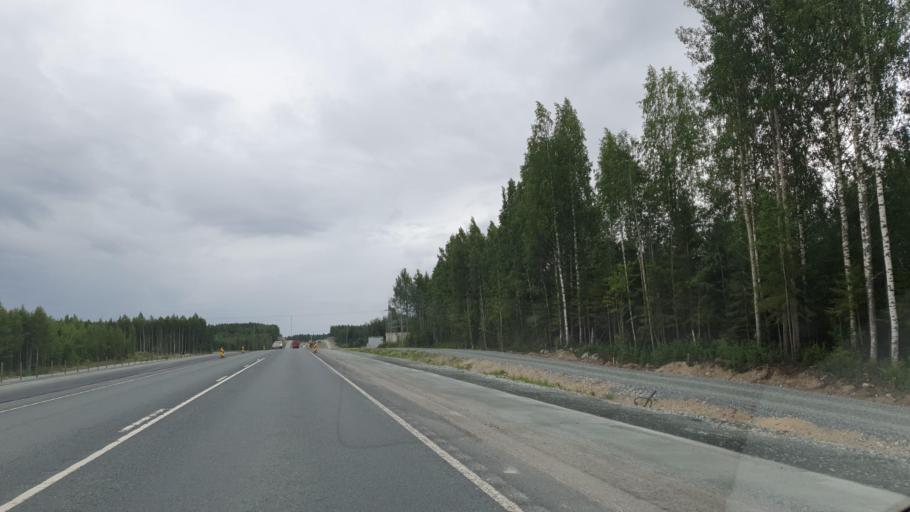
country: FI
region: Northern Savo
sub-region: Ylae-Savo
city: Lapinlahti
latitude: 63.2926
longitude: 27.4536
